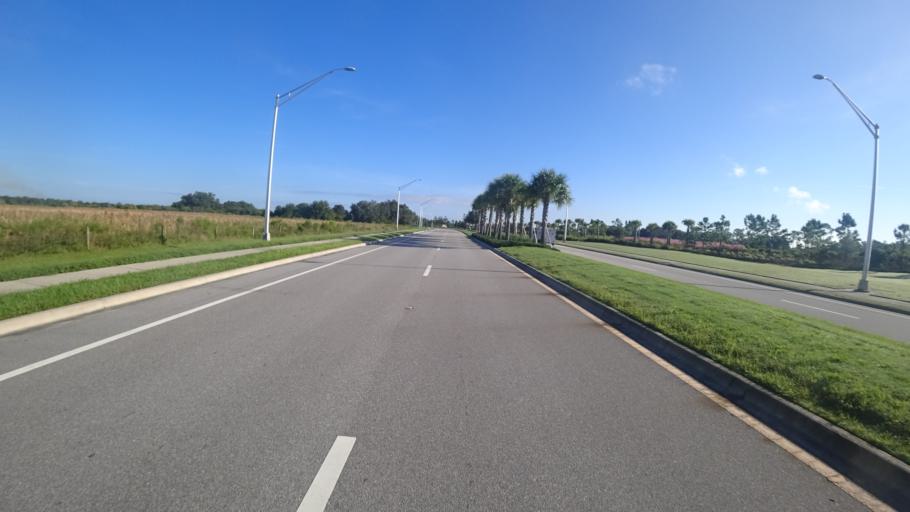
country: US
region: Florida
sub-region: Sarasota County
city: The Meadows
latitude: 27.4277
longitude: -82.3741
